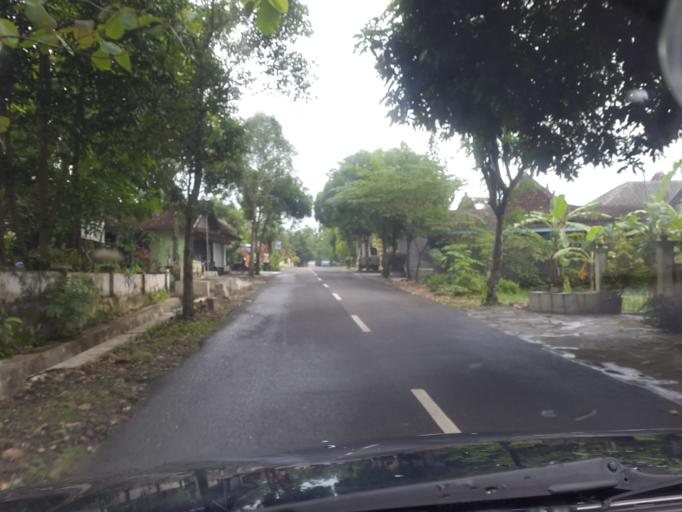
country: ID
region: Daerah Istimewa Yogyakarta
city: Wonosari
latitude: -8.0026
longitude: 110.5078
